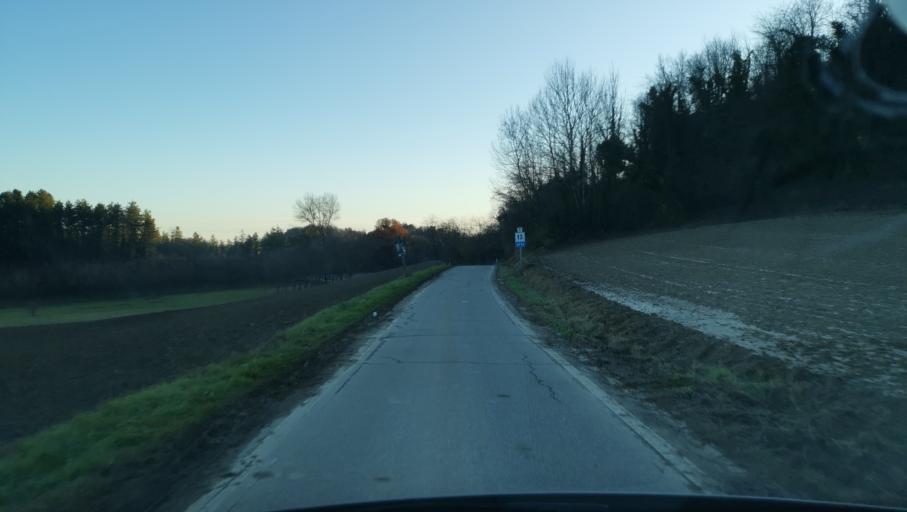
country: IT
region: Piedmont
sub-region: Provincia di Torino
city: Cinzano
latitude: 45.0876
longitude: 7.9253
